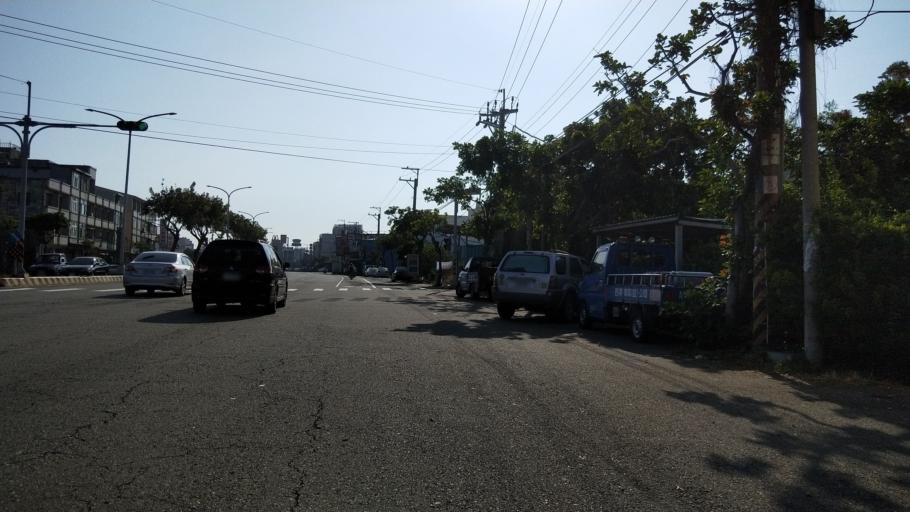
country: TW
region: Taiwan
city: Fengyuan
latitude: 24.2768
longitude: 120.5730
